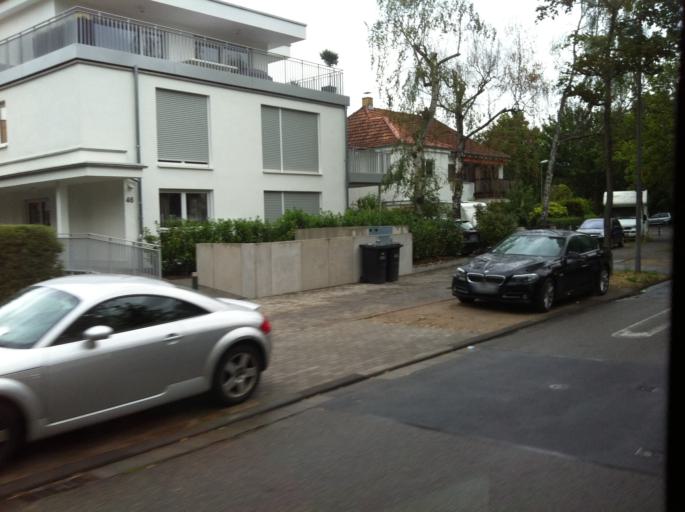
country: DE
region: Rheinland-Pfalz
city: Mainz
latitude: 50.0036
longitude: 8.2502
